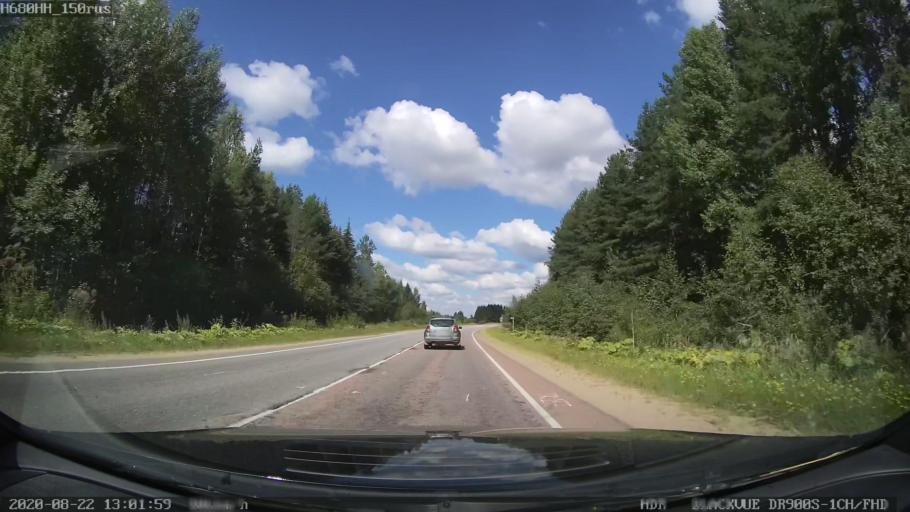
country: RU
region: Tverskaya
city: Bezhetsk
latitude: 57.6429
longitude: 36.3950
